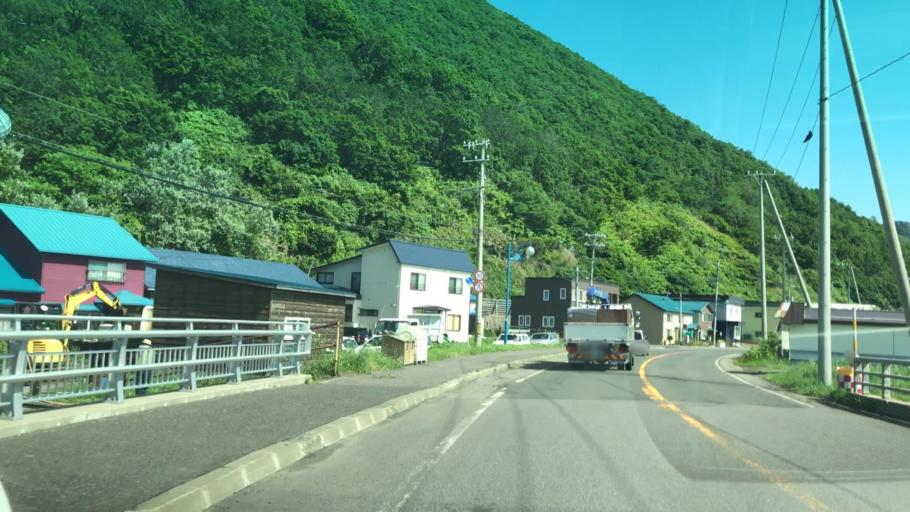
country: JP
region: Hokkaido
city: Iwanai
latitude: 43.1060
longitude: 140.4588
